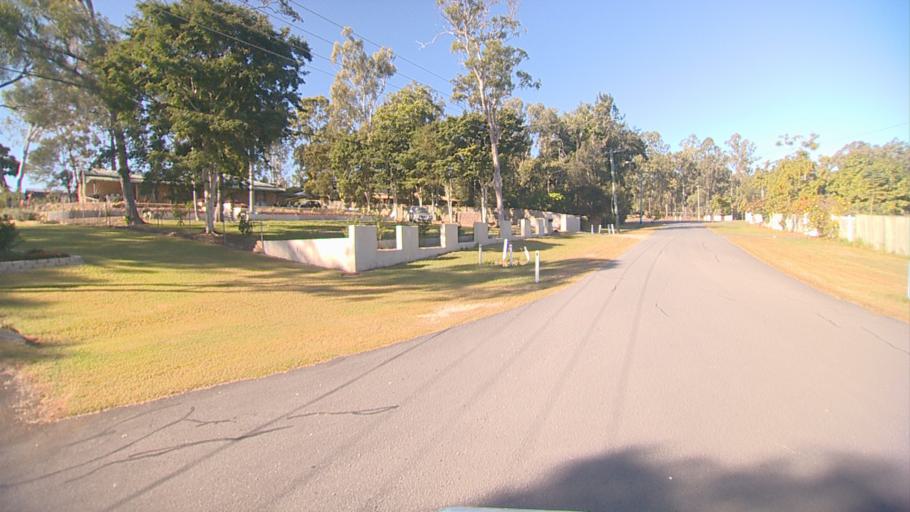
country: AU
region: Queensland
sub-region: Brisbane
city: Forest Lake
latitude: -27.6594
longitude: 153.0108
